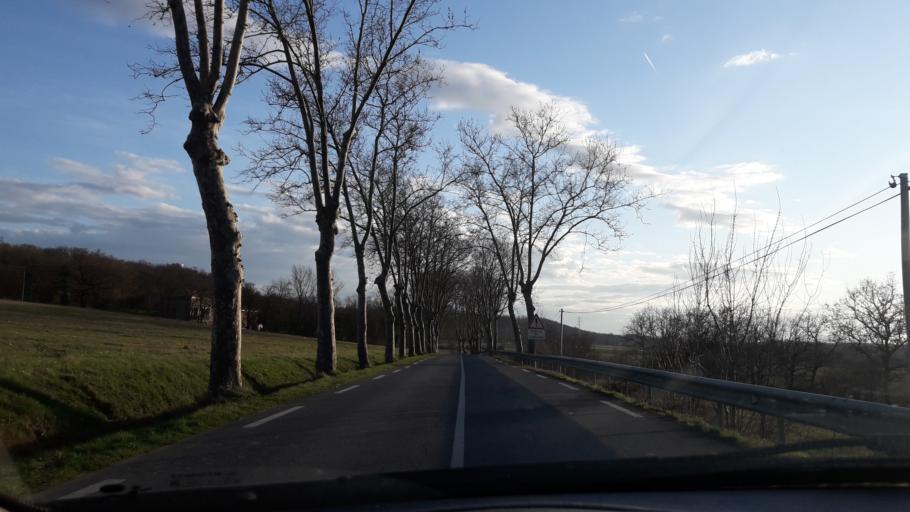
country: FR
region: Midi-Pyrenees
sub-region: Departement de la Haute-Garonne
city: Grenade
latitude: 43.7479
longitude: 1.2658
